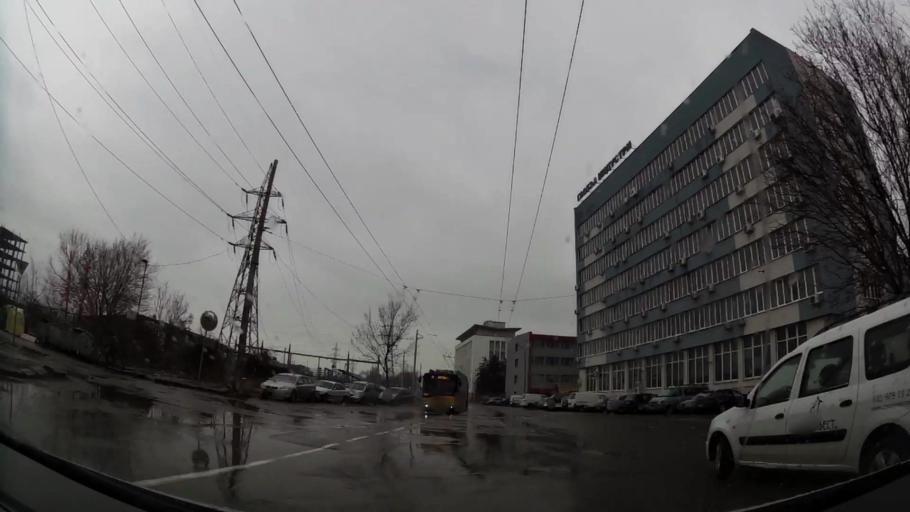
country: BG
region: Sofia-Capital
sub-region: Stolichna Obshtina
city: Sofia
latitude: 42.6712
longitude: 23.3867
